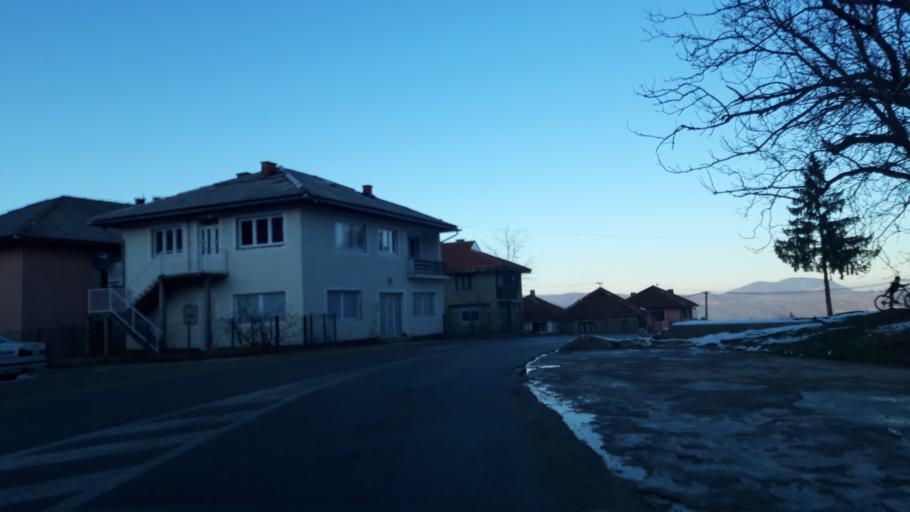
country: BA
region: Republika Srpska
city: Vlasenica
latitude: 44.1776
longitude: 18.9458
